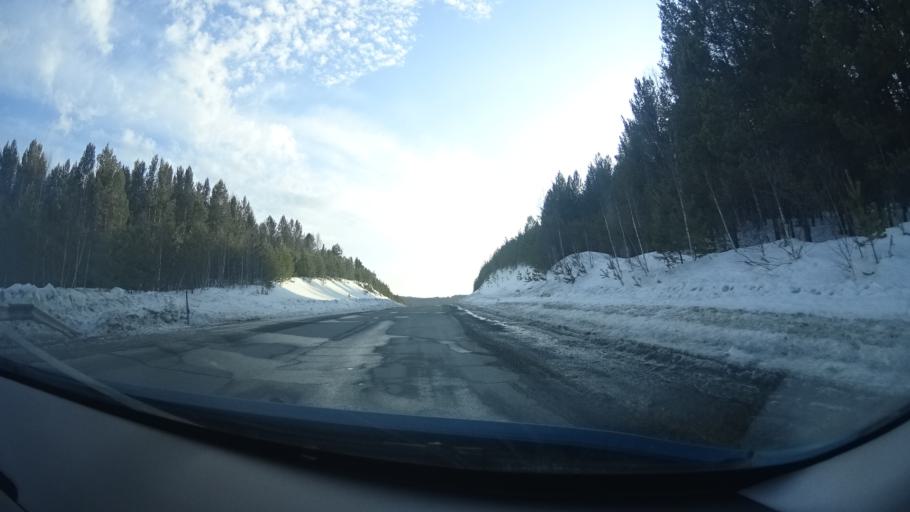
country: RU
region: Bashkortostan
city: Lomovka
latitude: 53.5983
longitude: 58.2019
